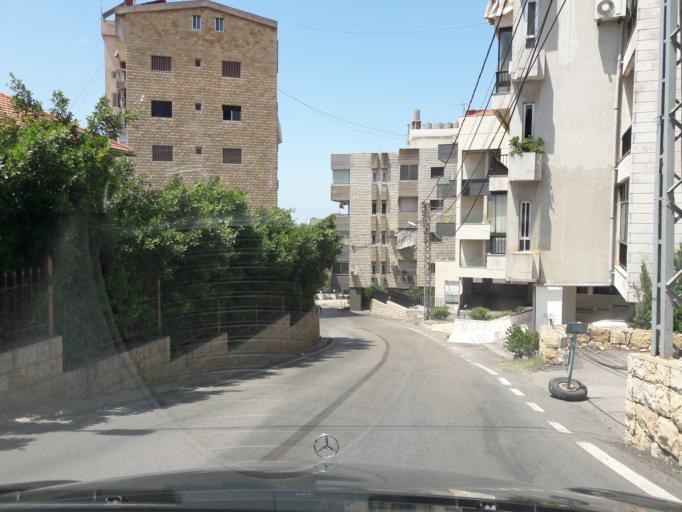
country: LB
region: Mont-Liban
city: Djounie
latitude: 33.9337
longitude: 35.6228
